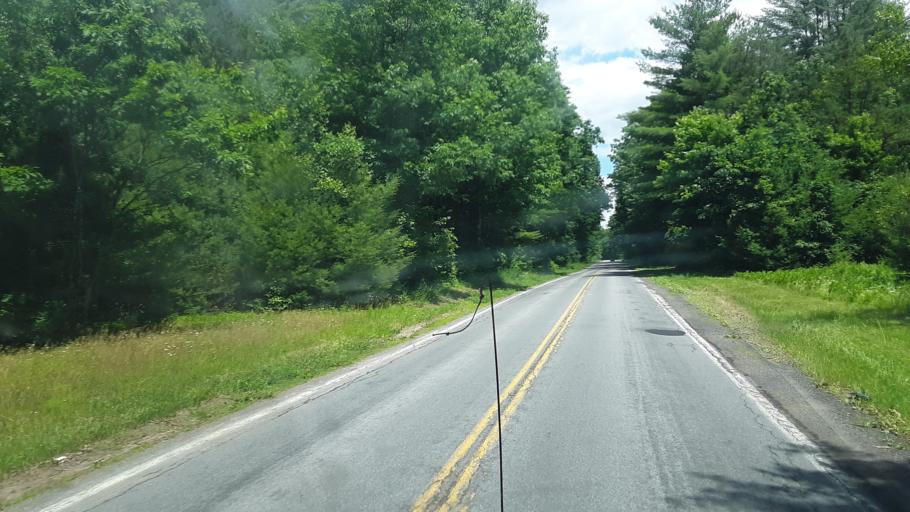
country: US
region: New York
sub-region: Oneida County
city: Rome
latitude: 43.2584
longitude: -75.5942
